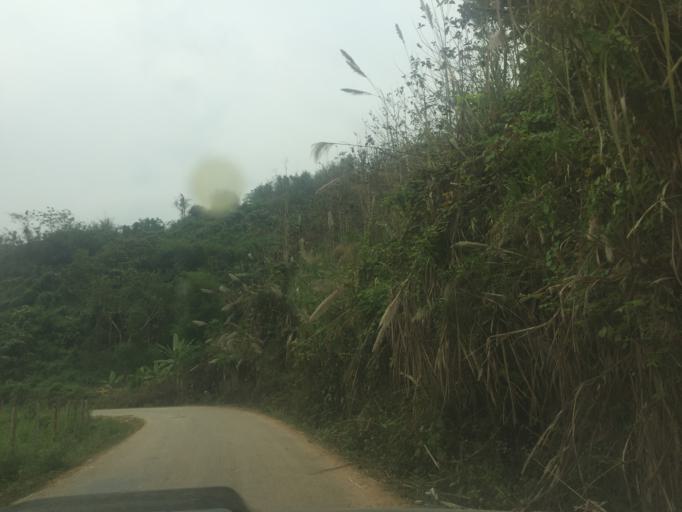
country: LA
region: Vientiane
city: Muang Sanakham
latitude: 18.3959
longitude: 101.5184
